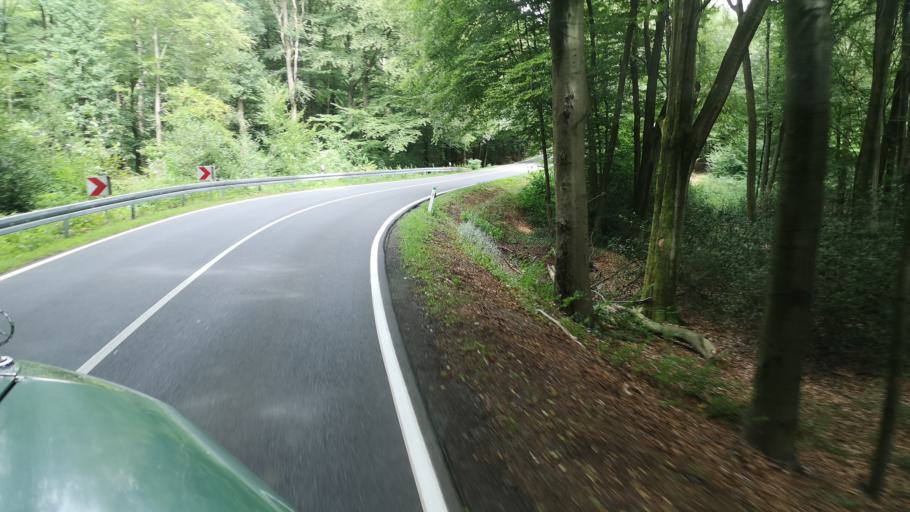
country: DE
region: North Rhine-Westphalia
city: Wermelskirchen
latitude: 51.1231
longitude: 7.2524
